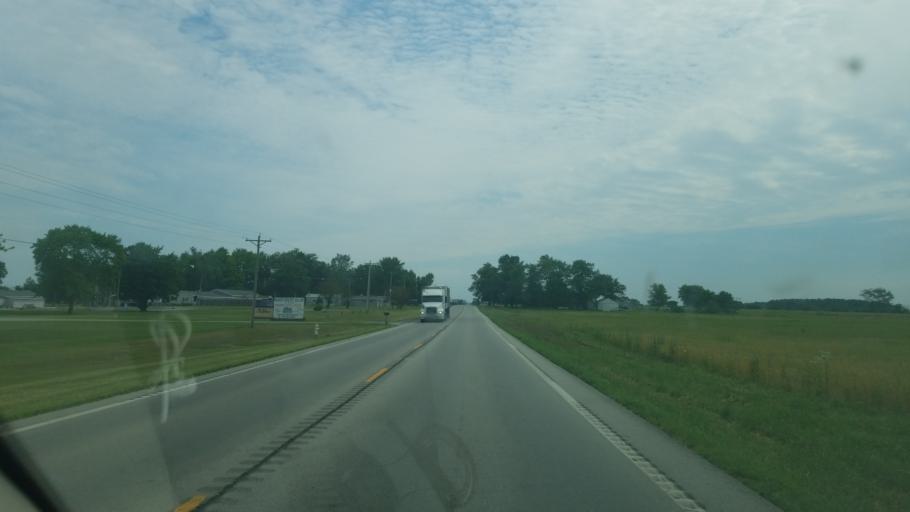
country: US
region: Ohio
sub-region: Seneca County
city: Fostoria
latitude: 41.1274
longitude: -83.4764
